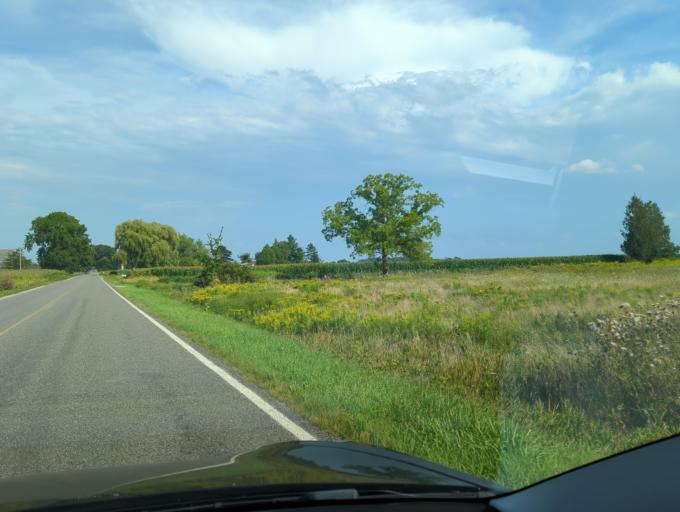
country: US
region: Michigan
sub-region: Ionia County
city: Ionia
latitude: 42.9297
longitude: -85.1044
